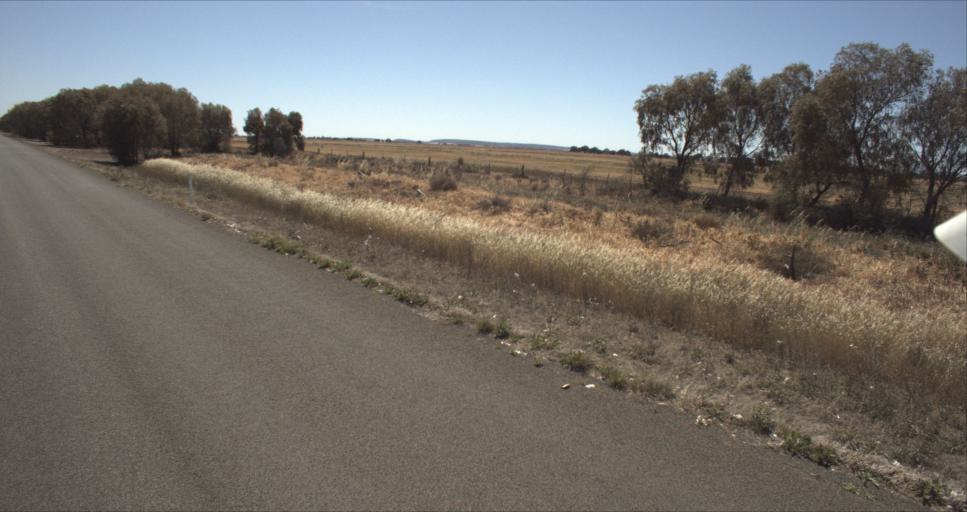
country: AU
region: New South Wales
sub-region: Leeton
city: Leeton
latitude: -34.4879
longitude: 146.2893
